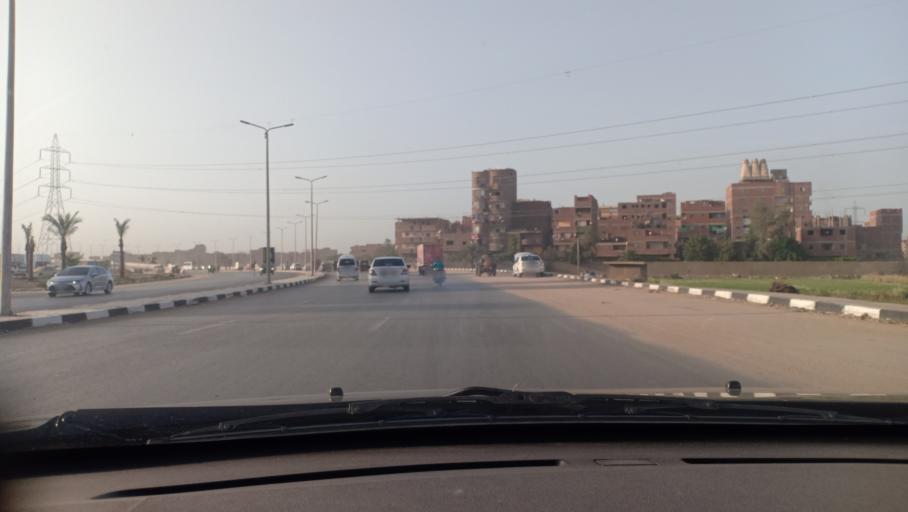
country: EG
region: Muhafazat al Qalyubiyah
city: Qalyub
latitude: 30.1397
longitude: 31.2643
